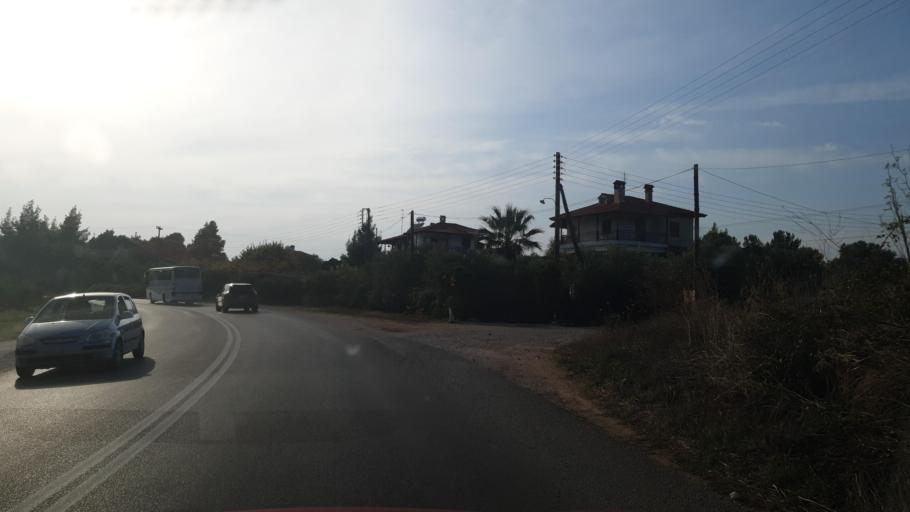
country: GR
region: Central Macedonia
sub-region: Nomos Chalkidikis
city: Nikiti
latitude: 40.2280
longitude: 23.6399
